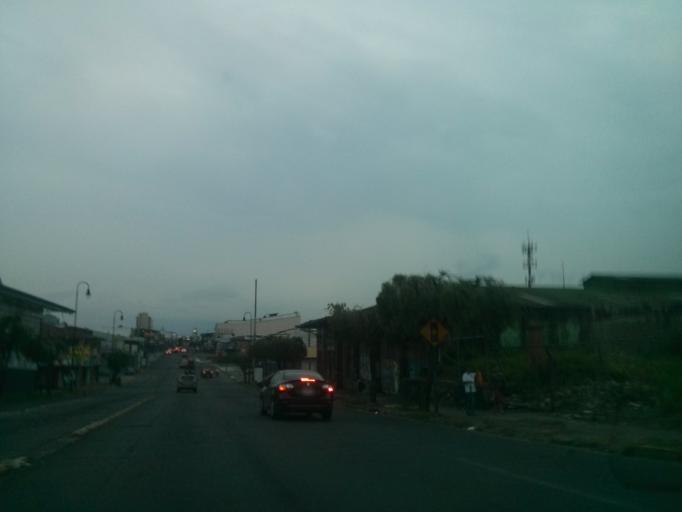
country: CR
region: San Jose
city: San Jose
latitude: 9.9297
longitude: -84.0868
